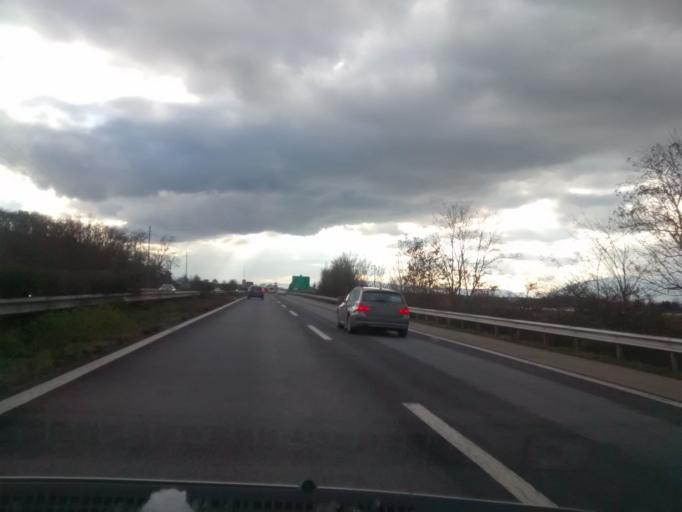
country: CH
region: Geneva
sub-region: Geneva
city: Bellevue
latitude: 46.2669
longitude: 6.1351
